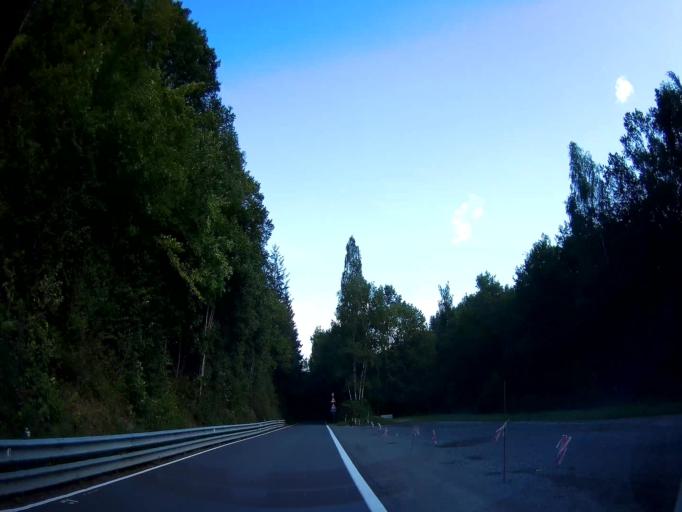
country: BE
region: Wallonia
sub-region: Province de Namur
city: Onhaye
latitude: 50.3045
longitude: 4.7714
